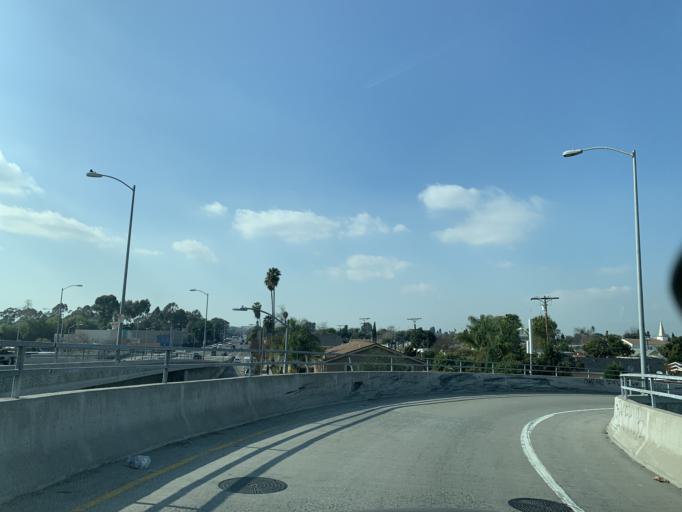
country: US
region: California
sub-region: Los Angeles County
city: Willowbrook
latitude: 33.9296
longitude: -118.2395
